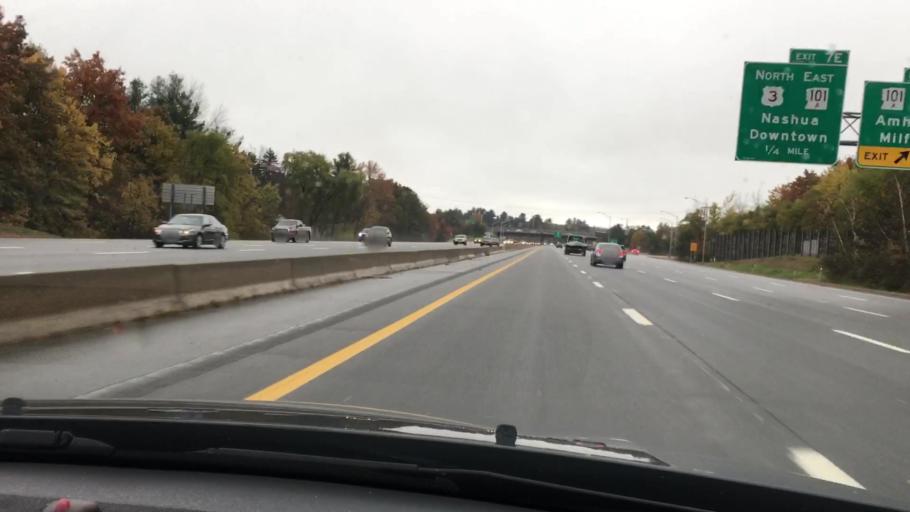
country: US
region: New Hampshire
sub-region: Hillsborough County
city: Nashua
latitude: 42.7822
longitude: -71.4942
